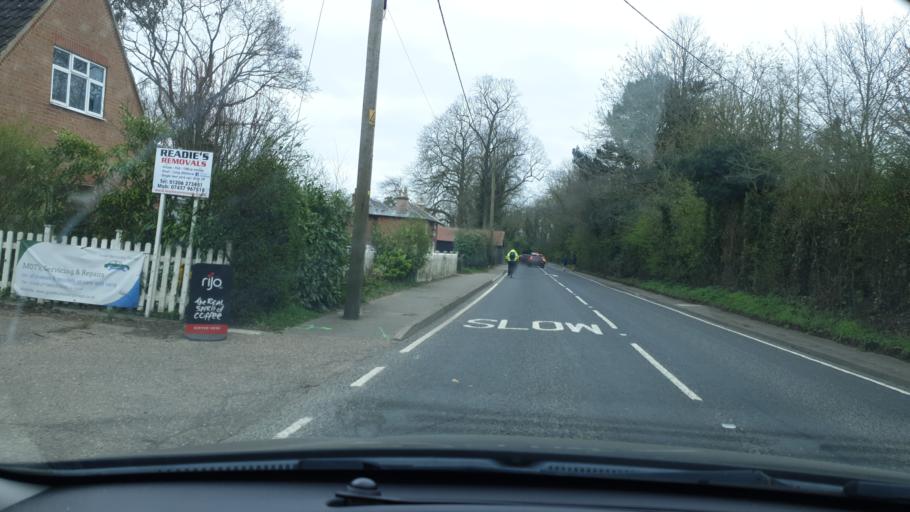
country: GB
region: England
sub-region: Essex
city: Great Horkesley
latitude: 51.9332
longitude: 0.8762
